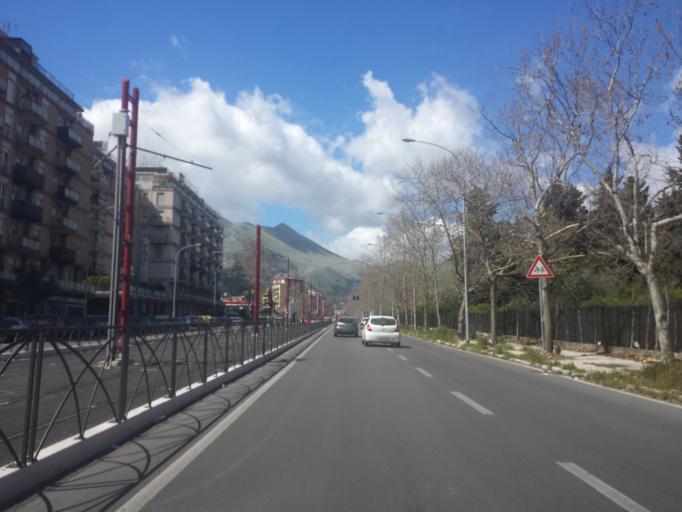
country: IT
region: Sicily
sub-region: Palermo
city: Palermo
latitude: 38.1270
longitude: 13.3202
